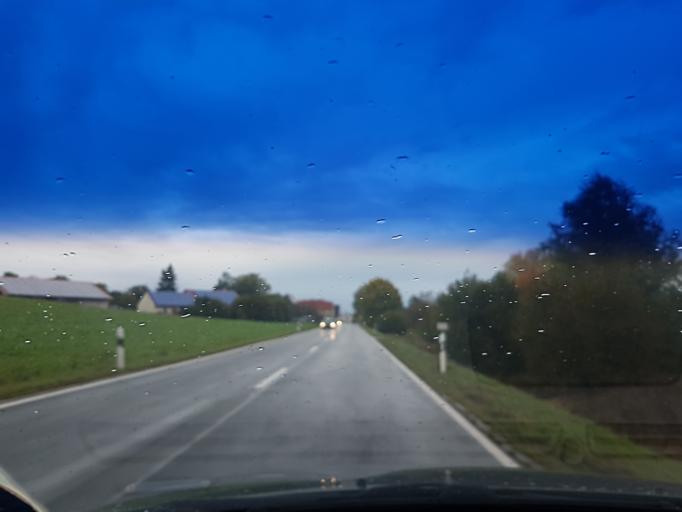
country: DE
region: Bavaria
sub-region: Regierungsbezirk Mittelfranken
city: Muhlhausen
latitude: 49.7616
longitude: 10.7916
